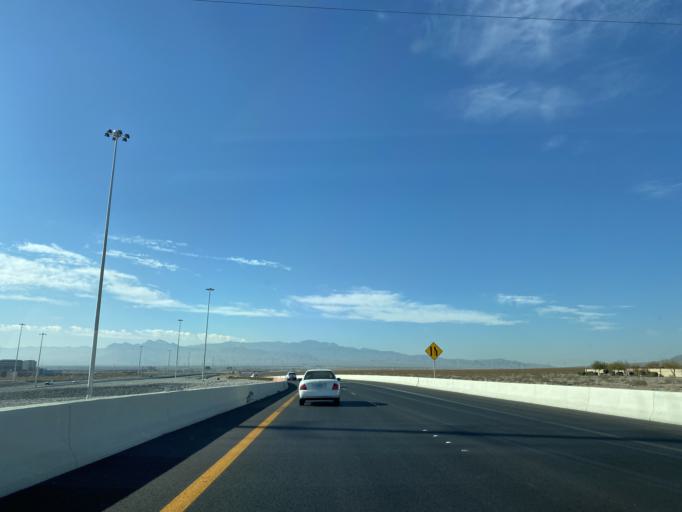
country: US
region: Nevada
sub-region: Clark County
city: Nellis Air Force Base
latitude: 36.2910
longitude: -115.0803
